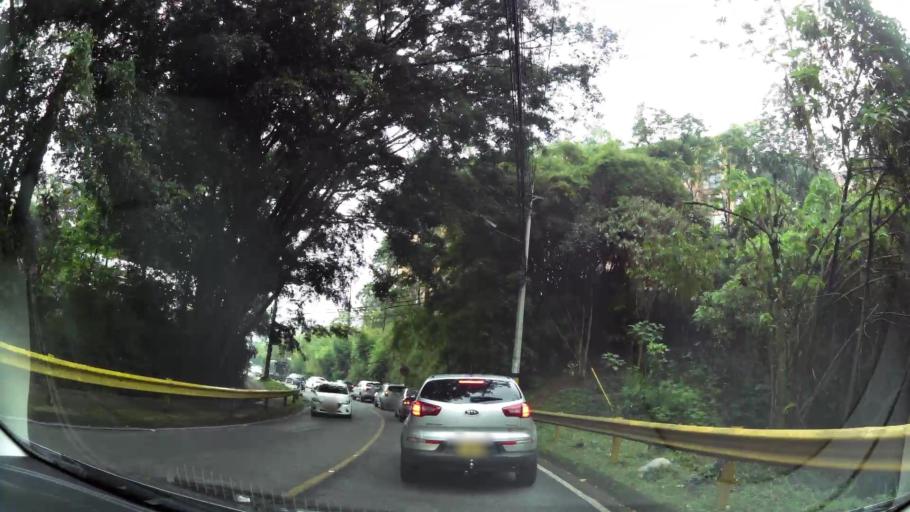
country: CO
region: Antioquia
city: Envigado
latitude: 6.1804
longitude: -75.5676
